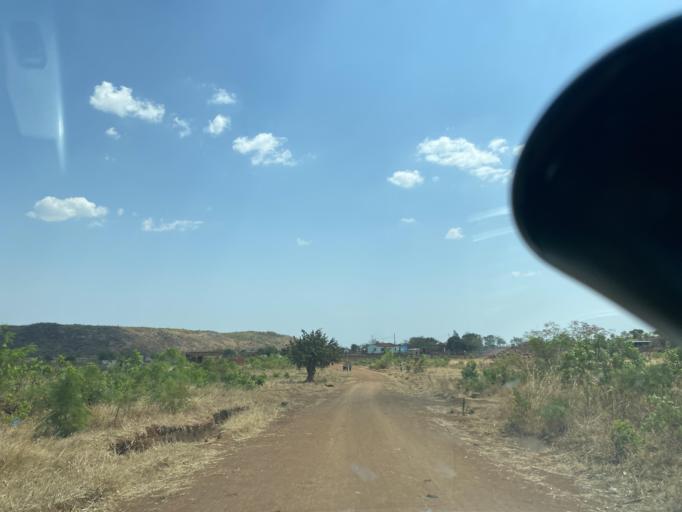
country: ZM
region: Lusaka
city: Kafue
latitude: -15.5036
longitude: 27.9422
